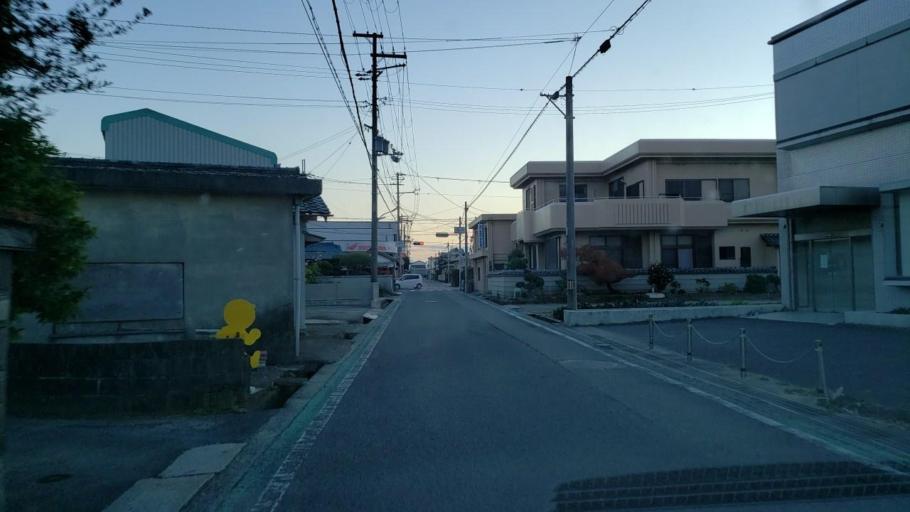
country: JP
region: Hyogo
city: Fukura
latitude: 34.3101
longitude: 134.7651
